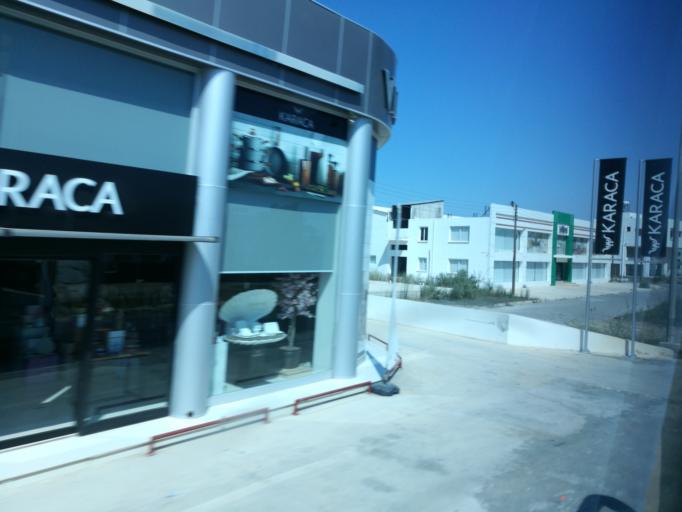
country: CY
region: Ammochostos
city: Famagusta
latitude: 35.1428
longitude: 33.9042
